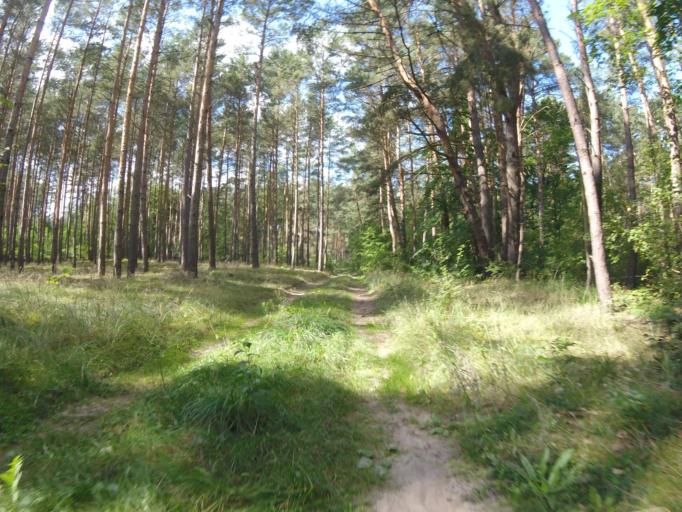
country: DE
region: Brandenburg
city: Schwerin
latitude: 52.1909
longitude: 13.5804
